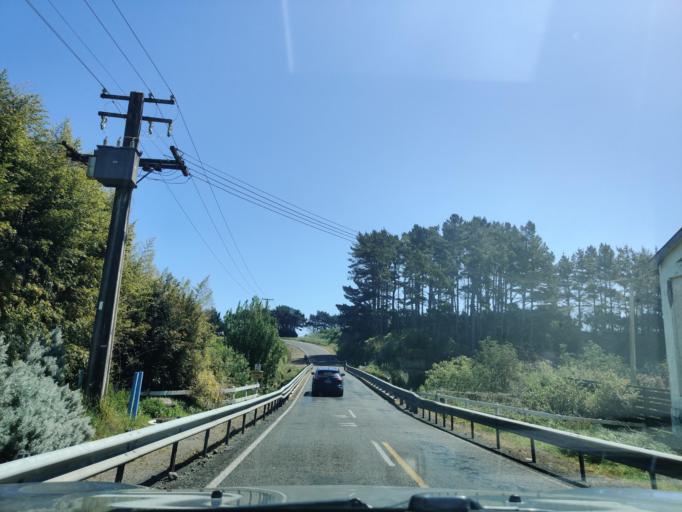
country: NZ
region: Taranaki
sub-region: South Taranaki District
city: Hawera
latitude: -39.5447
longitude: 174.0724
